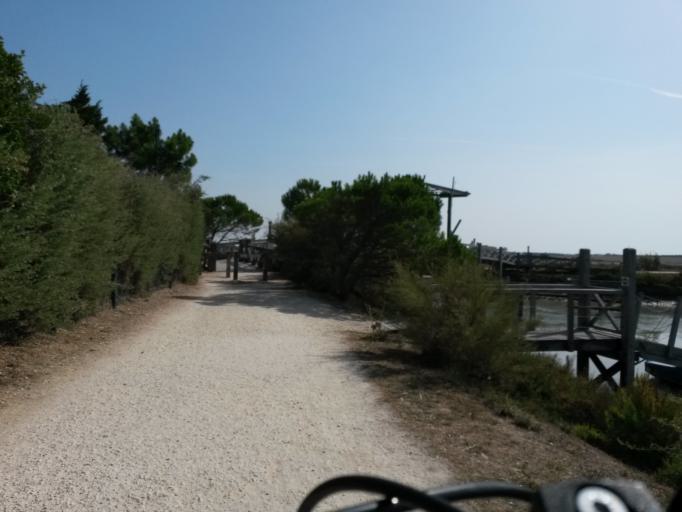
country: FR
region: Poitou-Charentes
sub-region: Departement de la Charente-Maritime
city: Nieul-sur-Mer
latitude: 46.2022
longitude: -1.2009
